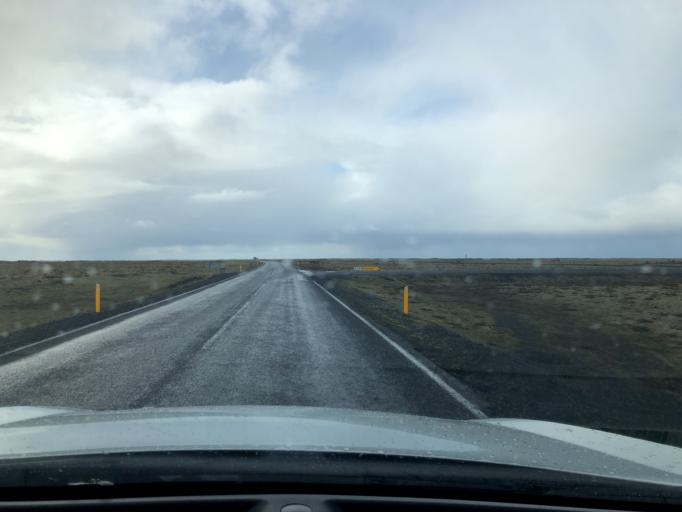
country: IS
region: South
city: Vestmannaeyjar
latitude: 63.5947
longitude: -18.4629
